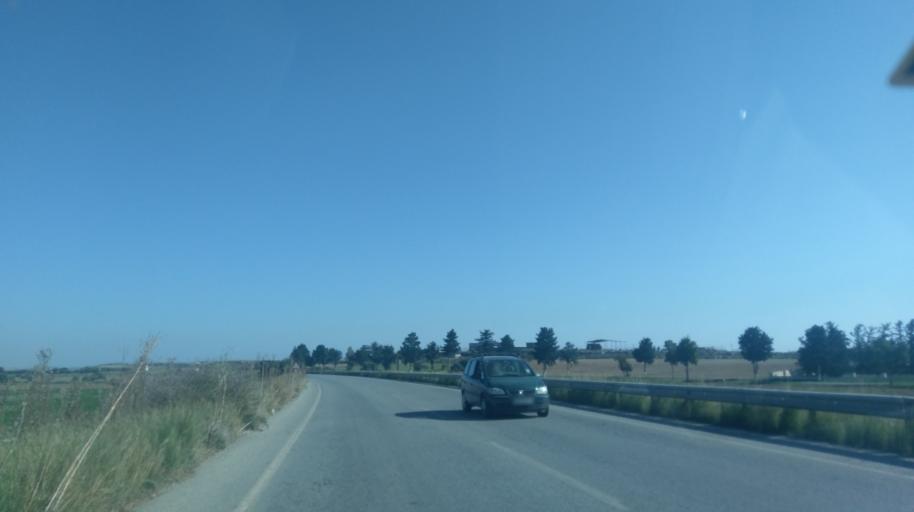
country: CY
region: Ammochostos
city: Lefkonoiko
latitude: 35.2633
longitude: 33.7934
